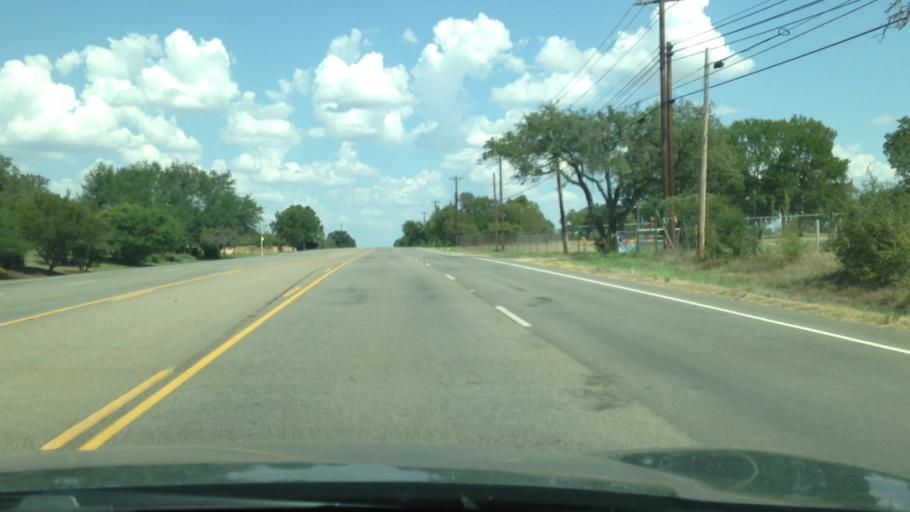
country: US
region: Texas
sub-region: Williamson County
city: Leander
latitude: 30.6360
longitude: -97.7903
